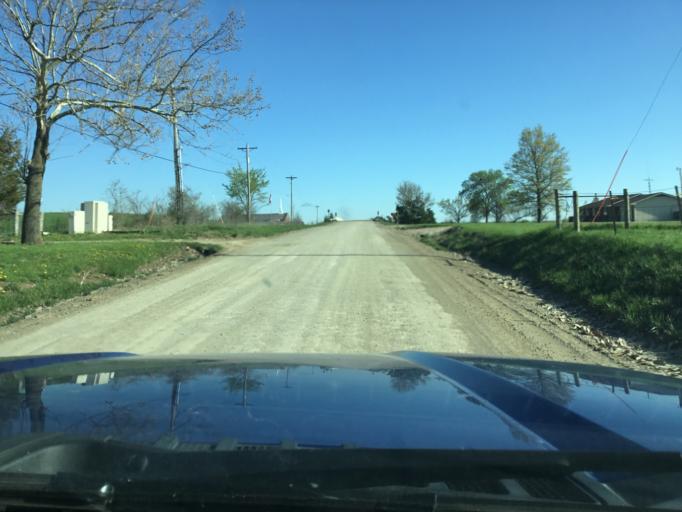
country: US
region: Kansas
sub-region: Douglas County
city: Lawrence
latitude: 38.9954
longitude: -95.3539
